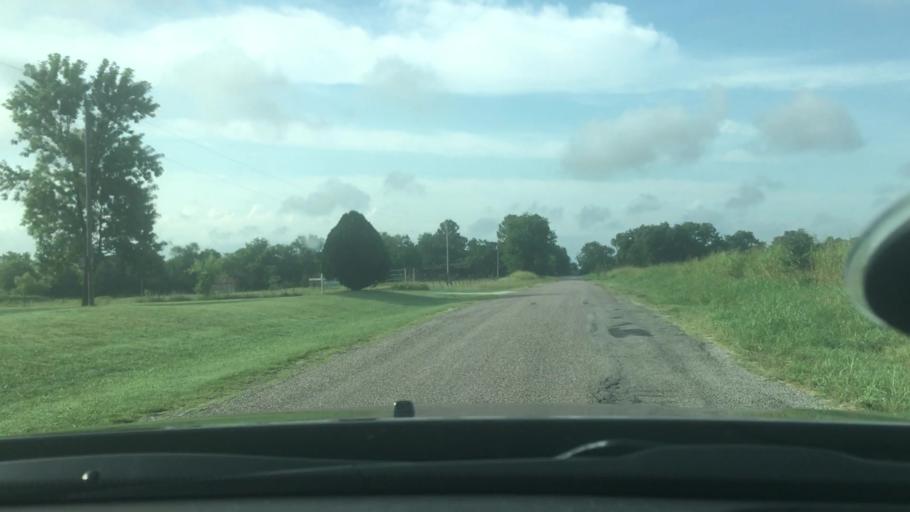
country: US
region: Oklahoma
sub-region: Pontotoc County
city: Ada
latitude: 34.6680
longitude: -96.5298
